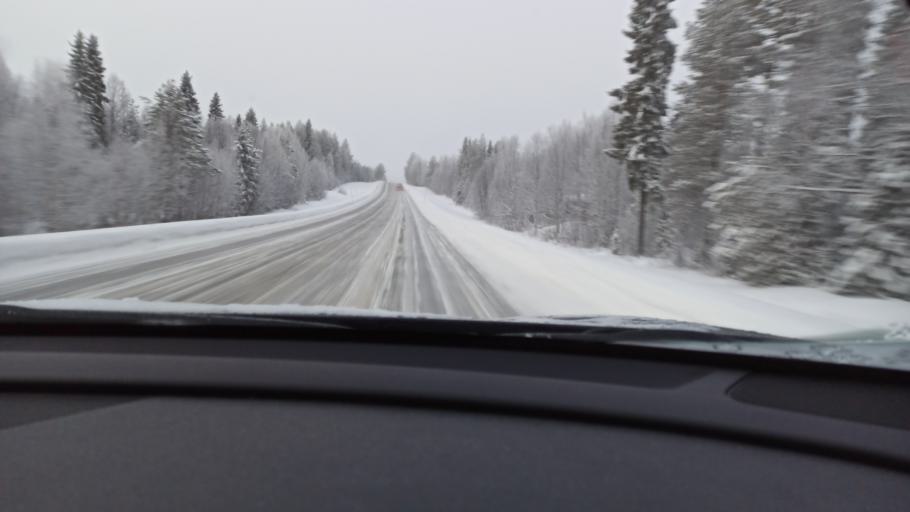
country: FI
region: Lapland
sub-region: Pohjois-Lappi
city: Sodankylae
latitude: 66.9285
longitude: 26.2332
